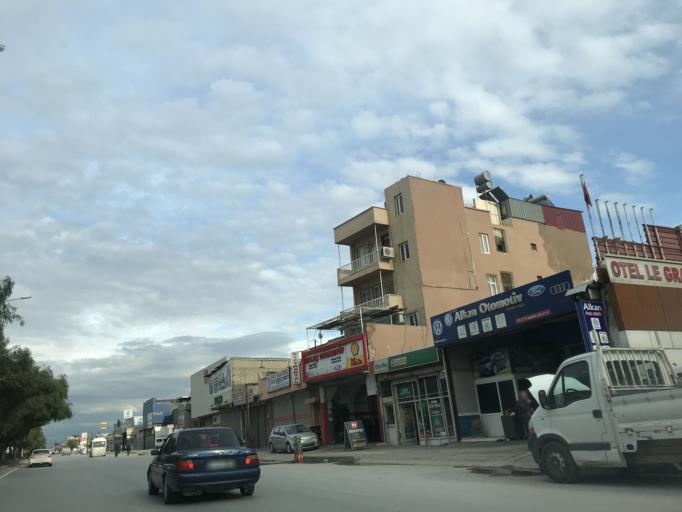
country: TR
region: Adana
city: Seyhan
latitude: 36.9957
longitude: 35.2679
